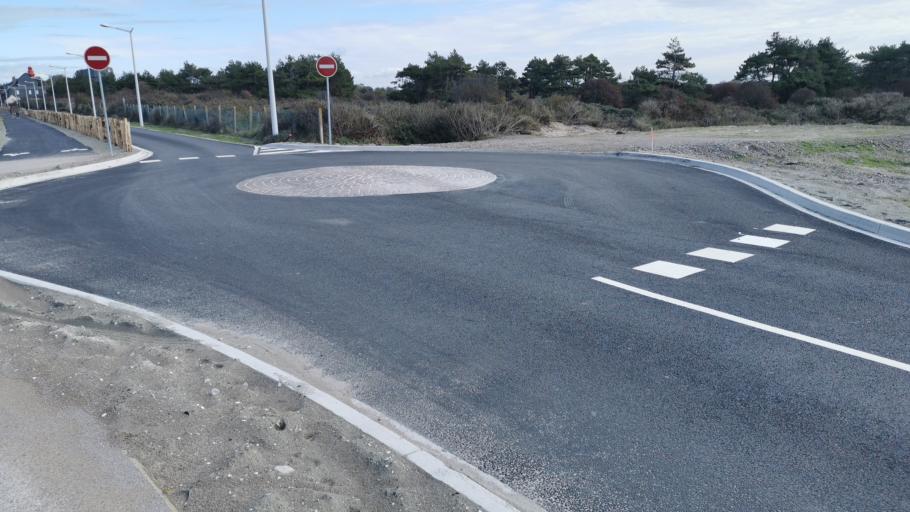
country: FR
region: Picardie
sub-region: Departement de la Somme
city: Cayeux-sur-Mer
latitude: 50.1900
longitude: 1.5051
